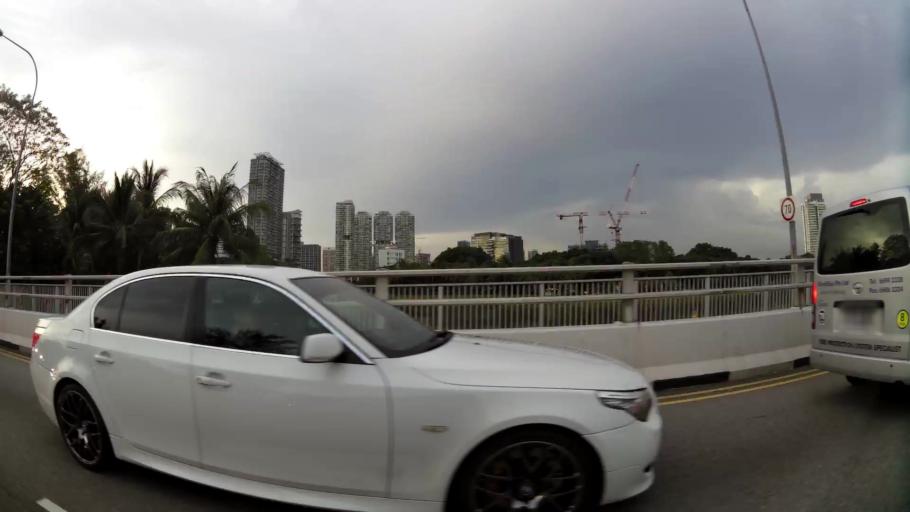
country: SG
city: Singapore
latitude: 1.3043
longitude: 103.8680
